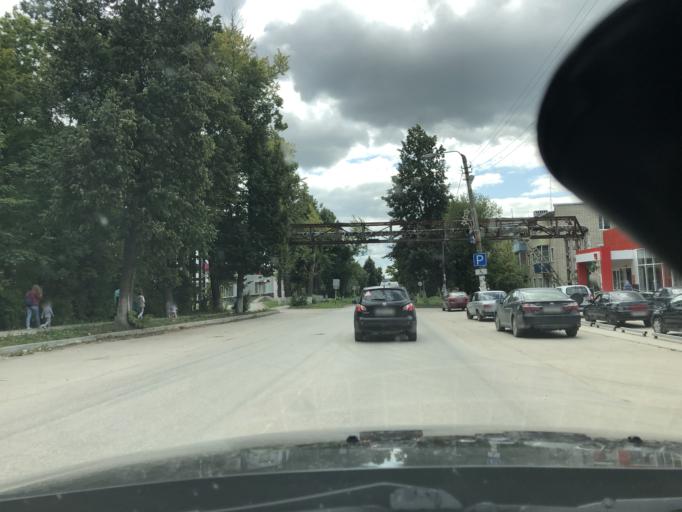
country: RU
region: Tula
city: Yasnogorsk
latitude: 54.4732
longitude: 37.6988
